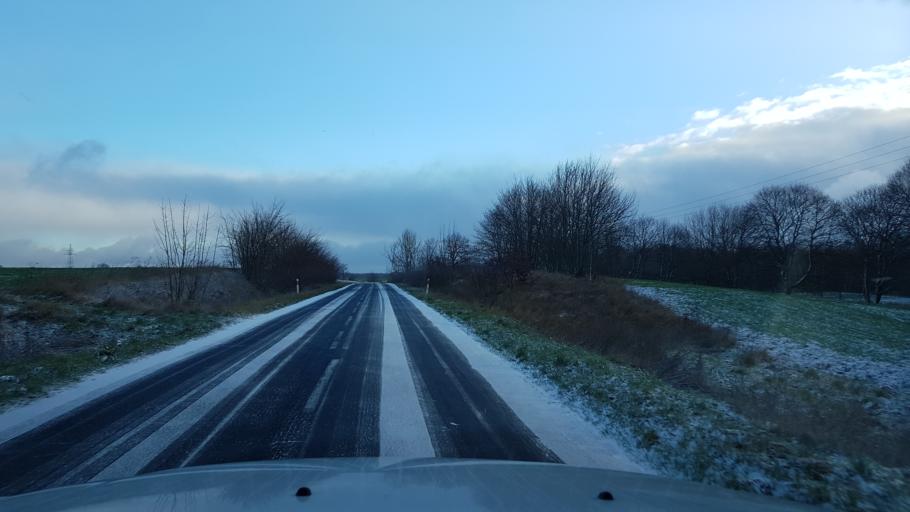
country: PL
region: West Pomeranian Voivodeship
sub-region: Powiat gryficki
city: Trzebiatow
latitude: 54.0396
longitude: 15.2162
